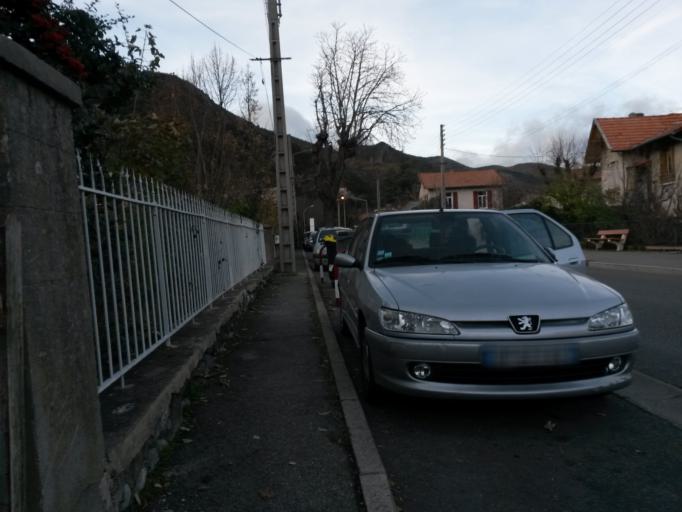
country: FR
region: Provence-Alpes-Cote d'Azur
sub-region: Departement des Alpes-de-Haute-Provence
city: Digne-les-Bains
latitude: 44.1005
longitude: 6.2312
